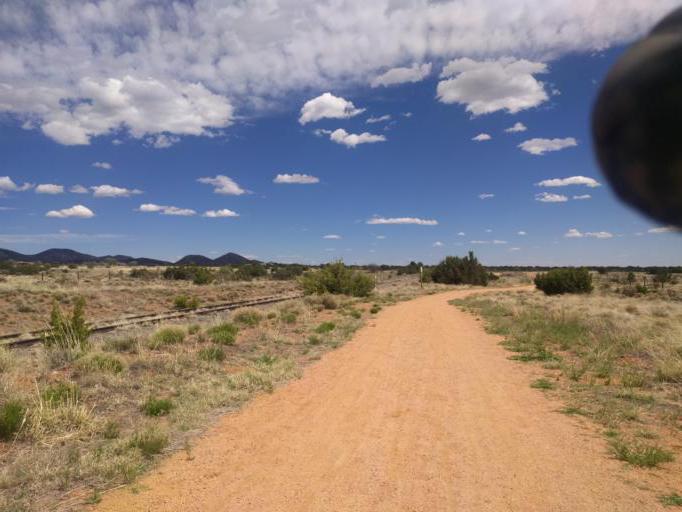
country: US
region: New Mexico
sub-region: Santa Fe County
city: Agua Fria
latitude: 35.6134
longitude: -105.9634
